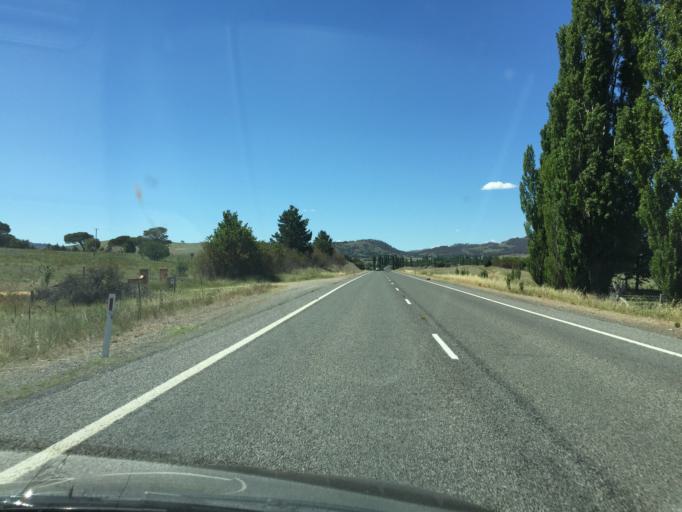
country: AU
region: Australian Capital Territory
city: Macarthur
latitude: -35.7160
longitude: 149.1586
